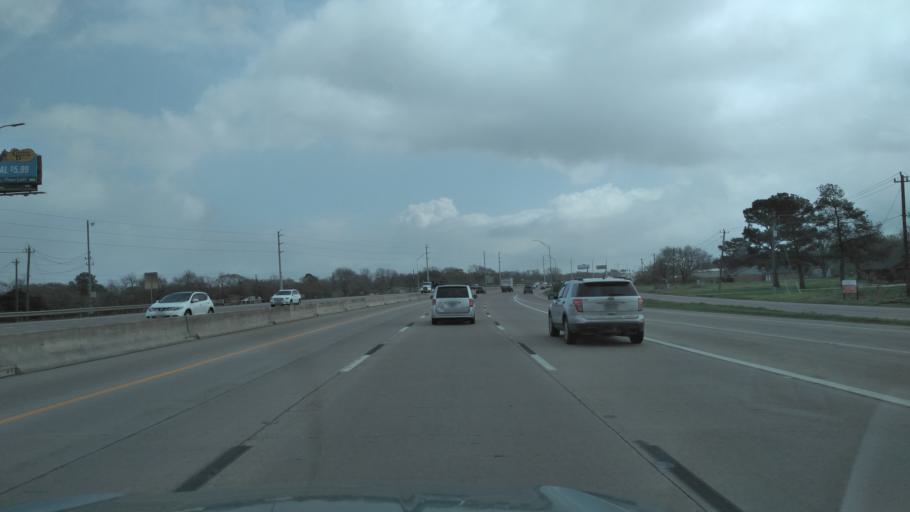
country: US
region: Texas
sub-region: Harris County
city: Highlands
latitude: 29.7994
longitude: -95.0275
